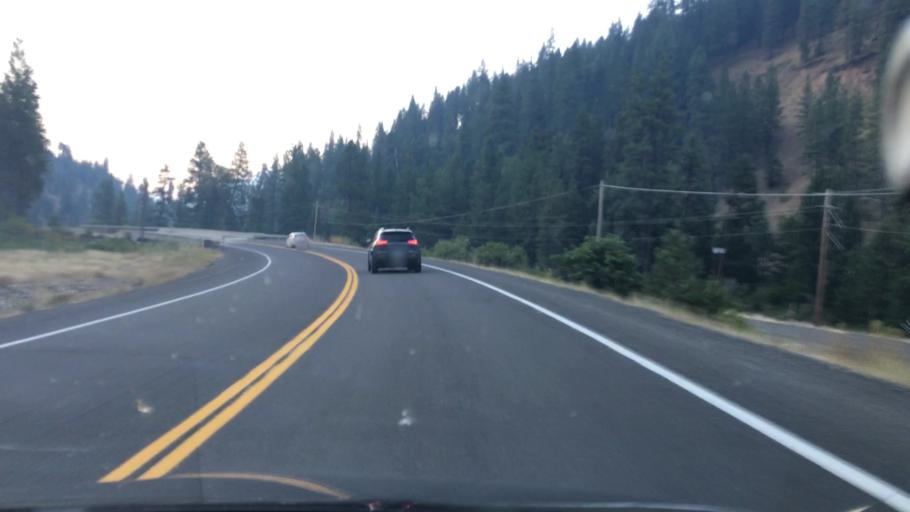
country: US
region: Idaho
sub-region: Valley County
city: McCall
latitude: 45.2020
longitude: -116.3108
